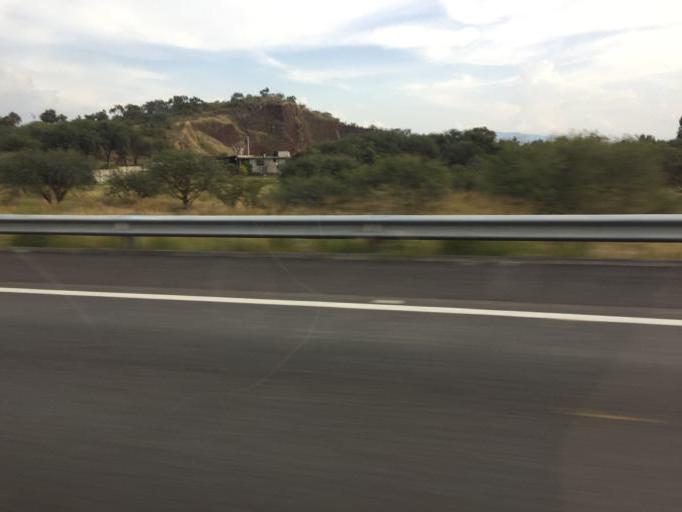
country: MX
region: Michoacan
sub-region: Alvaro Obregon
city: Tzintzimeo
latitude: 19.8911
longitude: -100.9860
